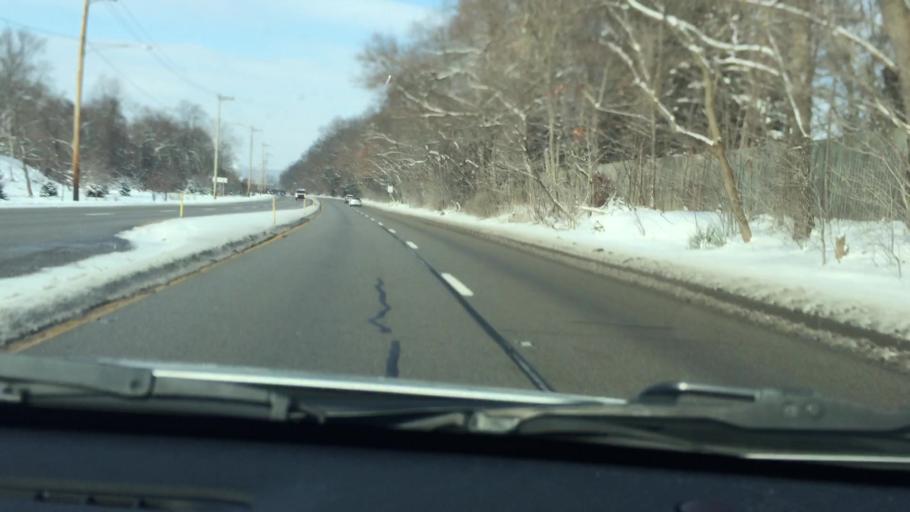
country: US
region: Pennsylvania
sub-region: Allegheny County
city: Edgeworth
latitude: 40.5495
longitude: -80.1970
